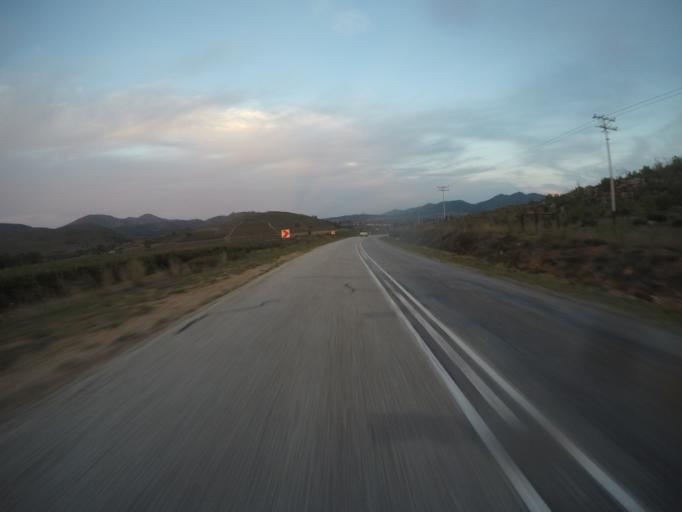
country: ZA
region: Western Cape
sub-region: Eden District Municipality
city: Plettenberg Bay
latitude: -33.7450
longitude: 23.4779
